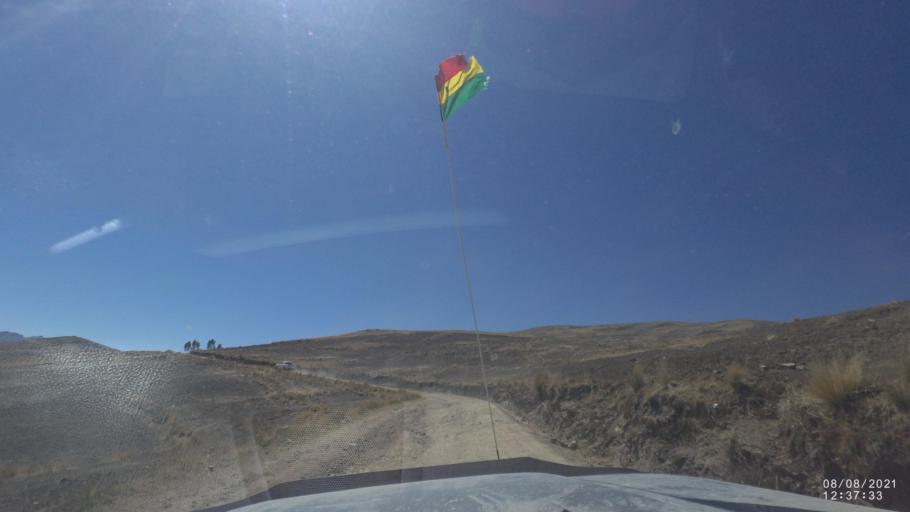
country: BO
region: Cochabamba
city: Colchani
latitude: -16.8373
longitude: -66.6268
